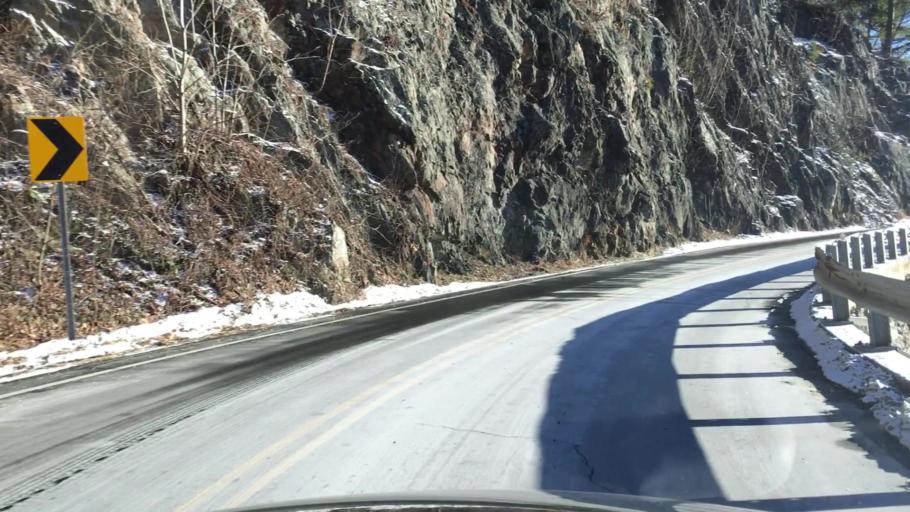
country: US
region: New Hampshire
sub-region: Grafton County
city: Woodsville
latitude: 44.1619
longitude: -72.0401
